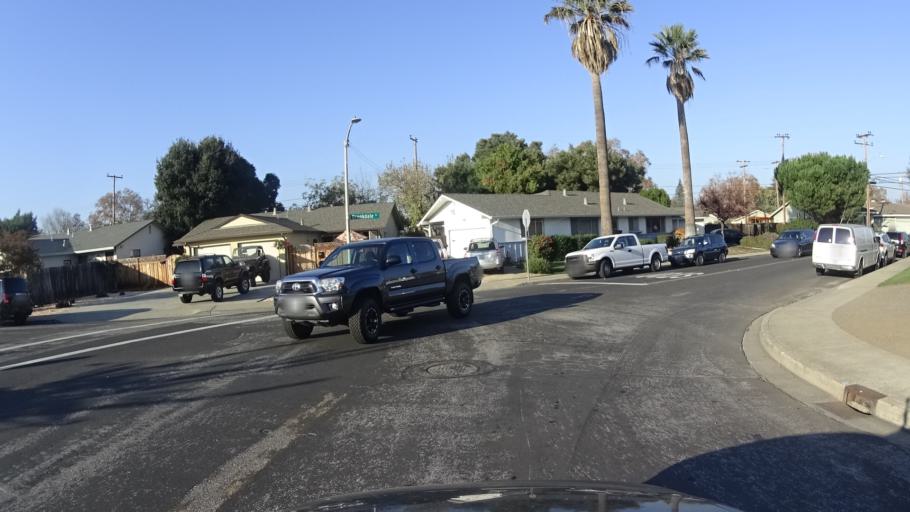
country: US
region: California
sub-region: Santa Clara County
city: Santa Clara
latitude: 37.3418
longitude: -121.9928
